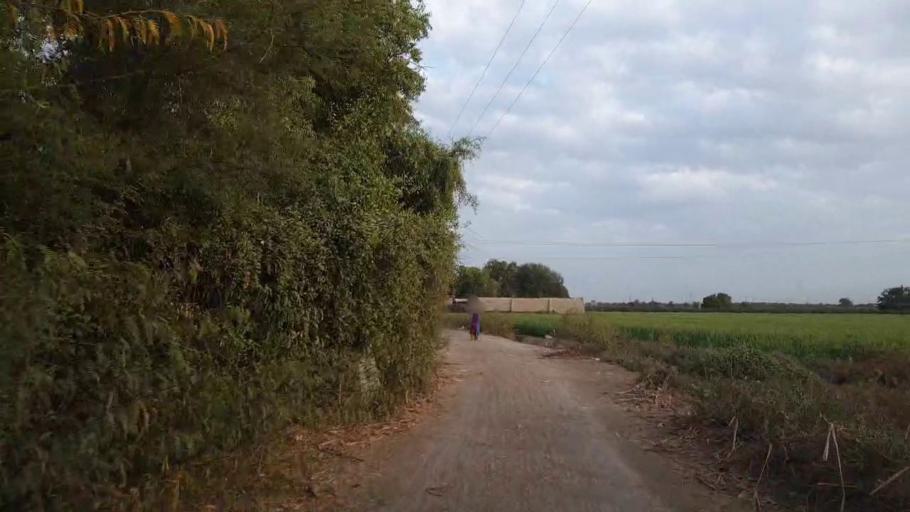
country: PK
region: Sindh
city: Matiari
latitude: 25.5706
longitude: 68.4387
